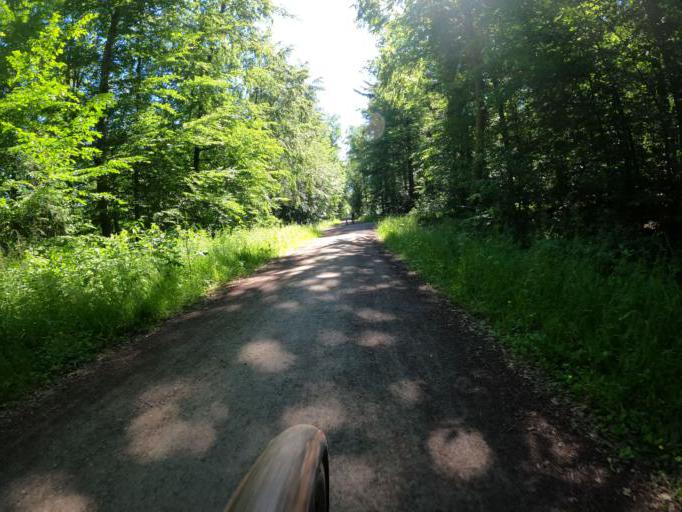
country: DE
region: Baden-Wuerttemberg
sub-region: Regierungsbezirk Stuttgart
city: Gerlingen
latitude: 48.7548
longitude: 9.1007
